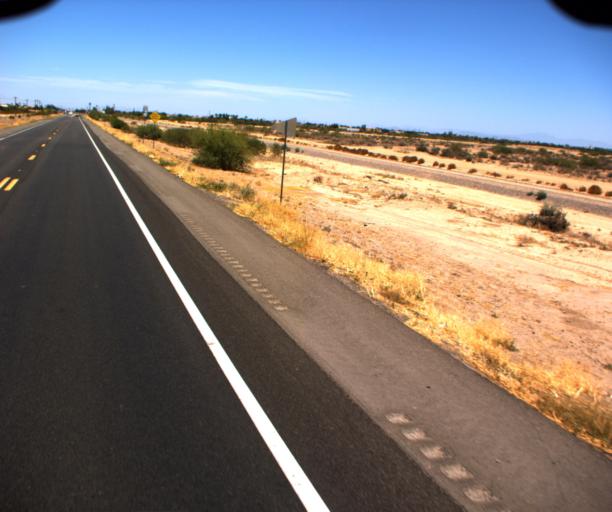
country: US
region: Arizona
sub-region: Maricopa County
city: Sun Lakes
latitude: 33.1959
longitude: -111.8409
